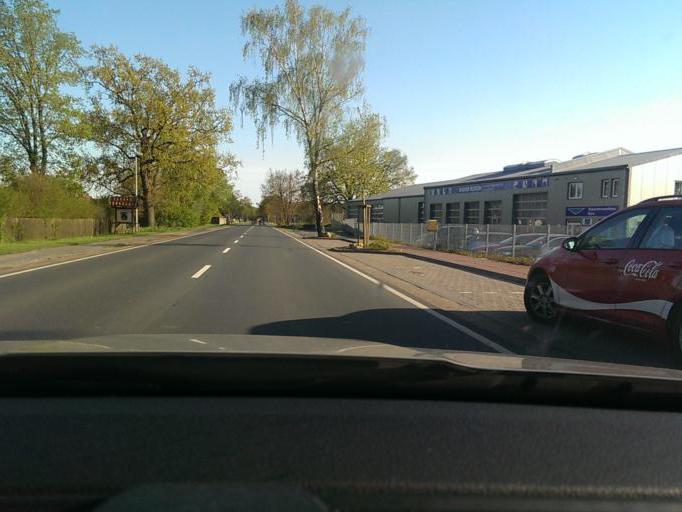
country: DE
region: Lower Saxony
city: Elze
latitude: 52.6019
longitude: 9.7245
